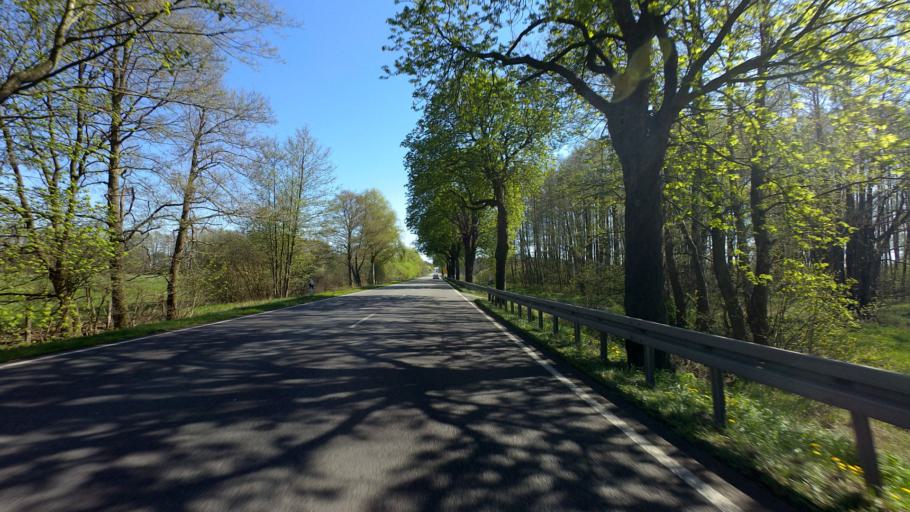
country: DE
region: Saxony-Anhalt
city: Klotze
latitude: 52.6907
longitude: 11.2635
